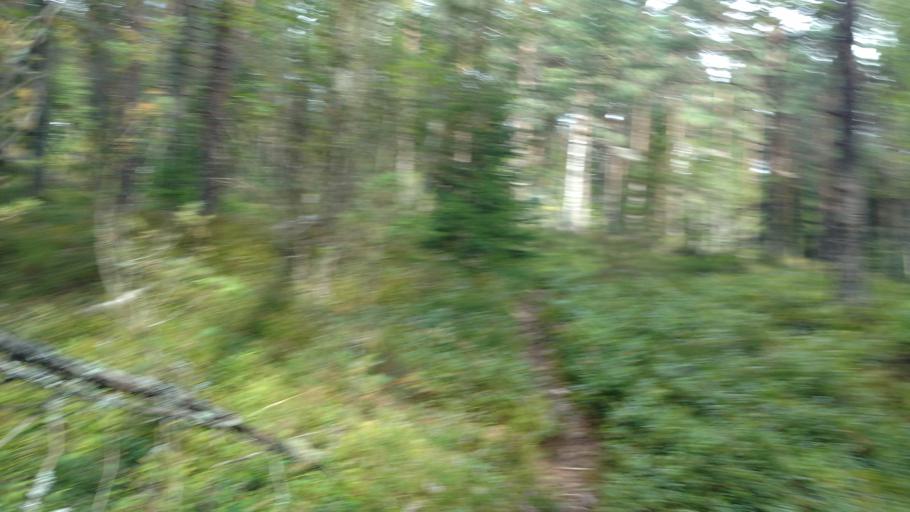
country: FI
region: Varsinais-Suomi
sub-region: Salo
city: Salo
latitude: 60.3577
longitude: 23.1671
